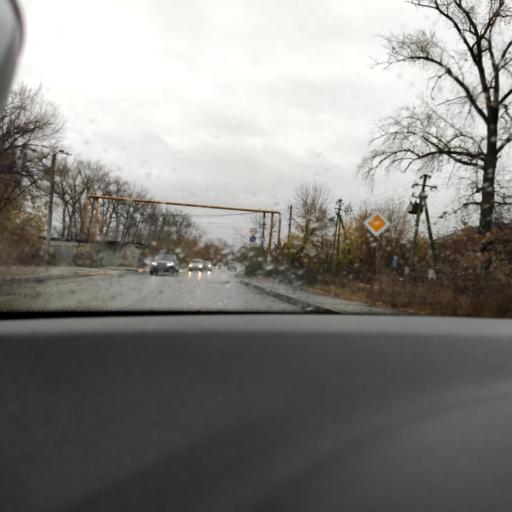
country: RU
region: Samara
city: Samara
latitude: 53.1575
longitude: 50.0806
